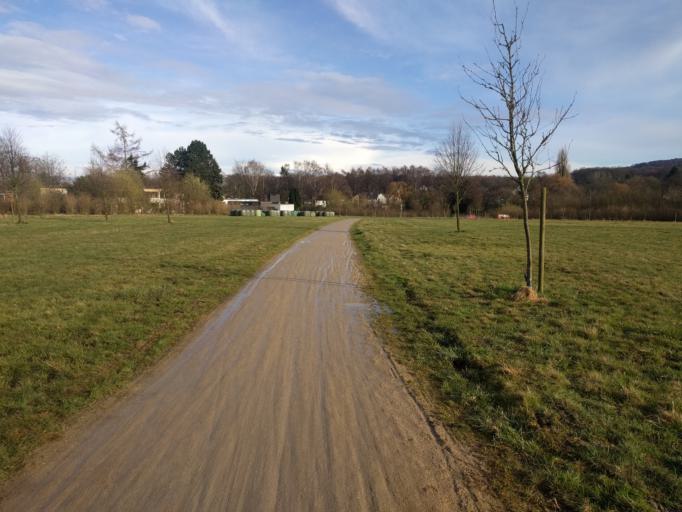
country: DE
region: North Rhine-Westphalia
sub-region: Regierungsbezirk Detmold
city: Bielefeld
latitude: 52.0453
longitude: 8.4960
